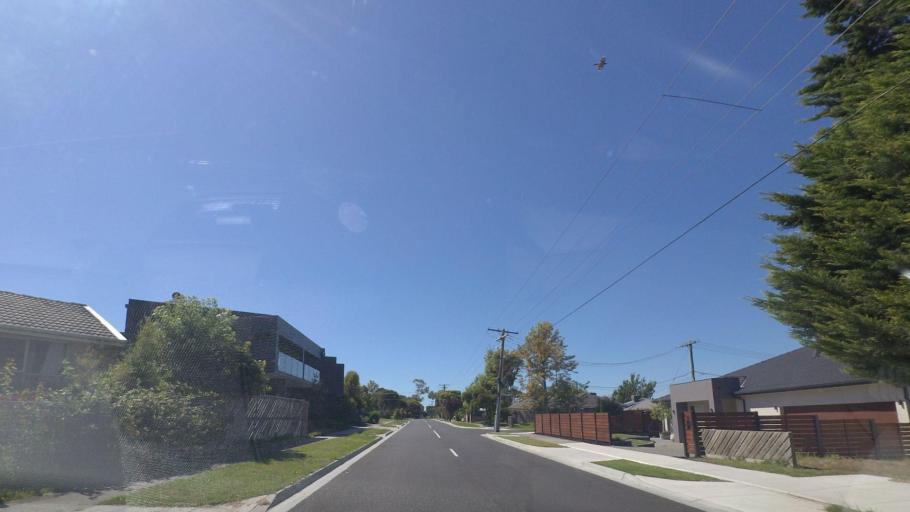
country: AU
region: Victoria
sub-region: Knox
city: Knoxfield
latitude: -37.8860
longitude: 145.2717
